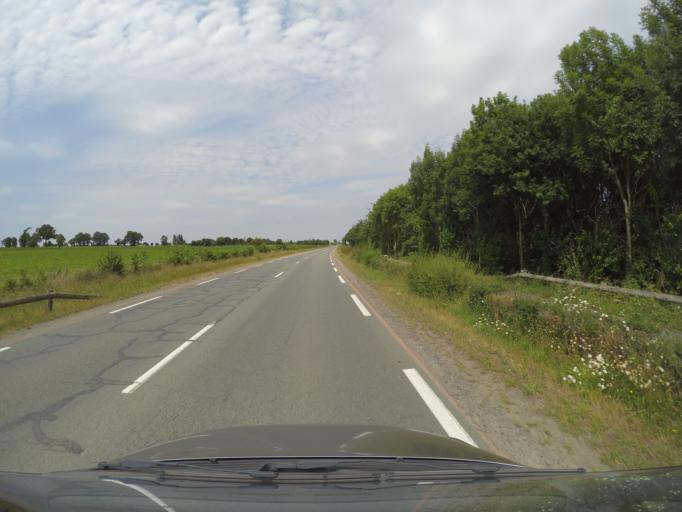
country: FR
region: Pays de la Loire
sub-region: Departement de la Vendee
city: Les Herbiers
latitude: 46.8449
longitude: -1.0096
